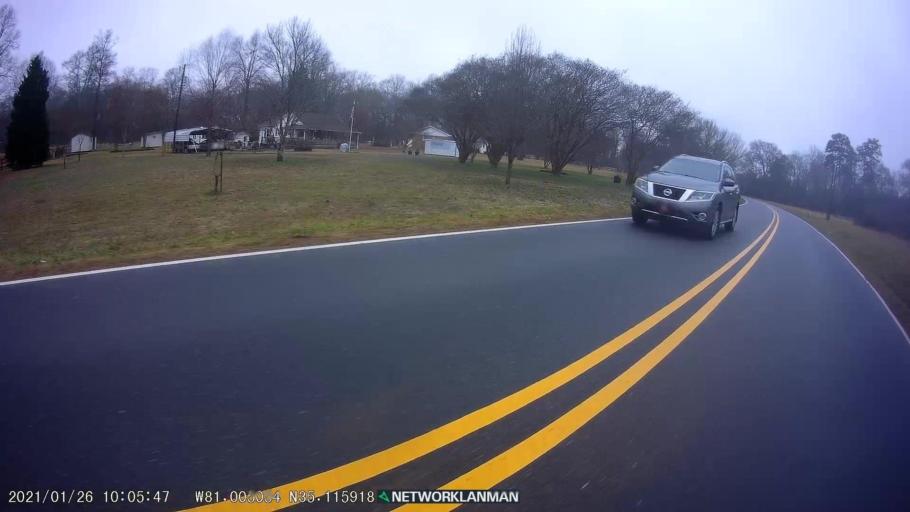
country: US
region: South Carolina
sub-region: York County
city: Lake Wylie
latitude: 35.1161
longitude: -81.0052
